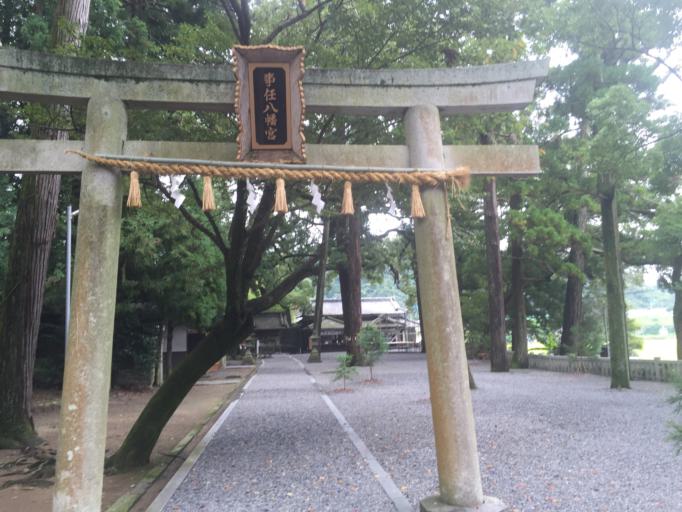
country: JP
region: Shizuoka
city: Kanaya
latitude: 34.7984
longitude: 138.0748
